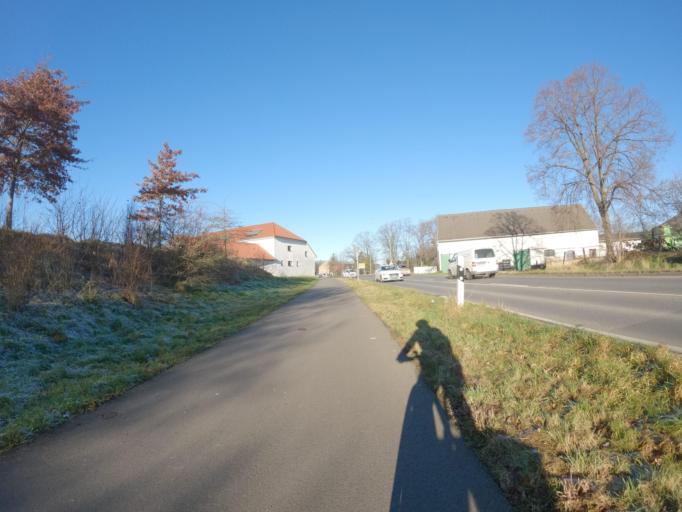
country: DE
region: North Rhine-Westphalia
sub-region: Regierungsbezirk Koln
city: Aachen
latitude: 50.8093
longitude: 6.0928
